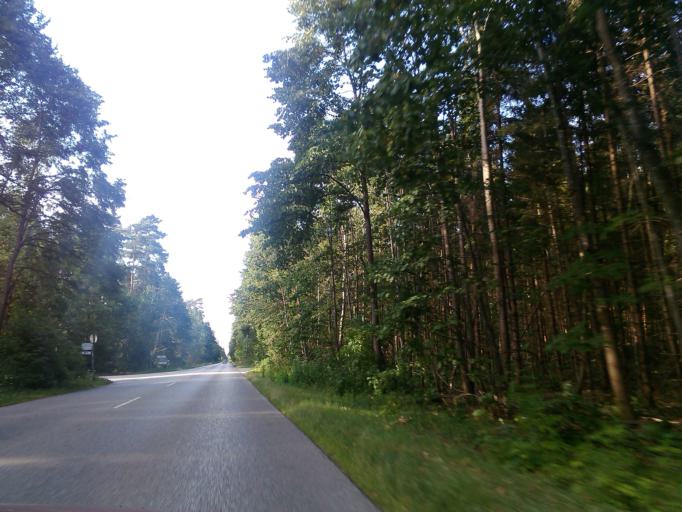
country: DE
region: Bavaria
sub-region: Upper Bavaria
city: Krailling
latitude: 48.1020
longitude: 11.3742
